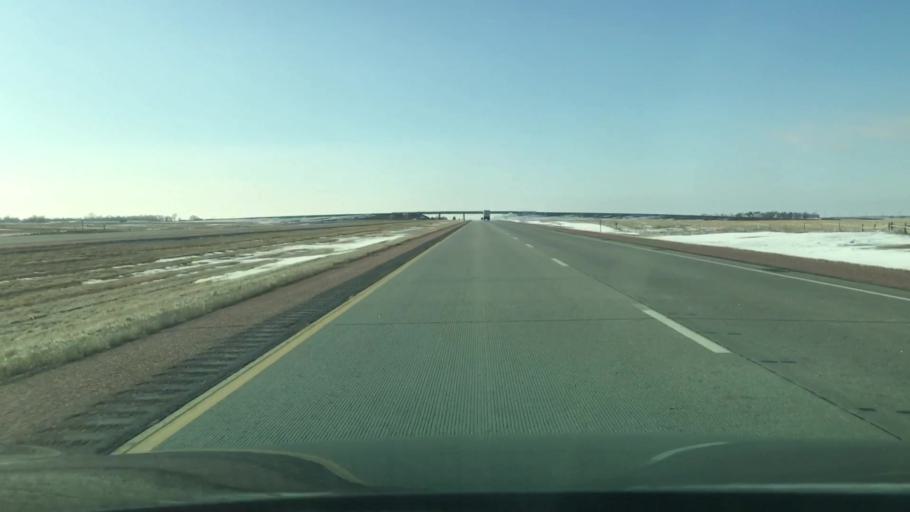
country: US
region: South Dakota
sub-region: Aurora County
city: Plankinton
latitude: 43.7076
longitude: -98.5163
